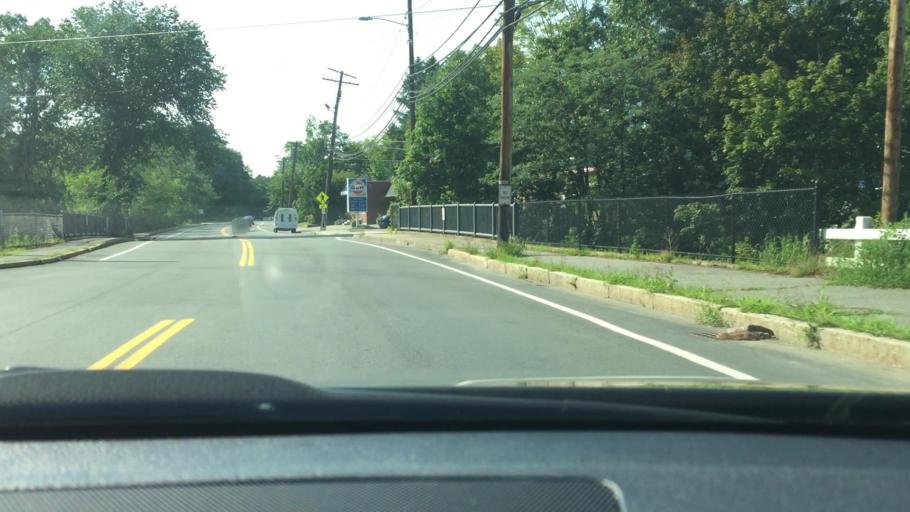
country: US
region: Massachusetts
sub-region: Norfolk County
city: Needham
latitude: 42.2756
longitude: -71.2144
